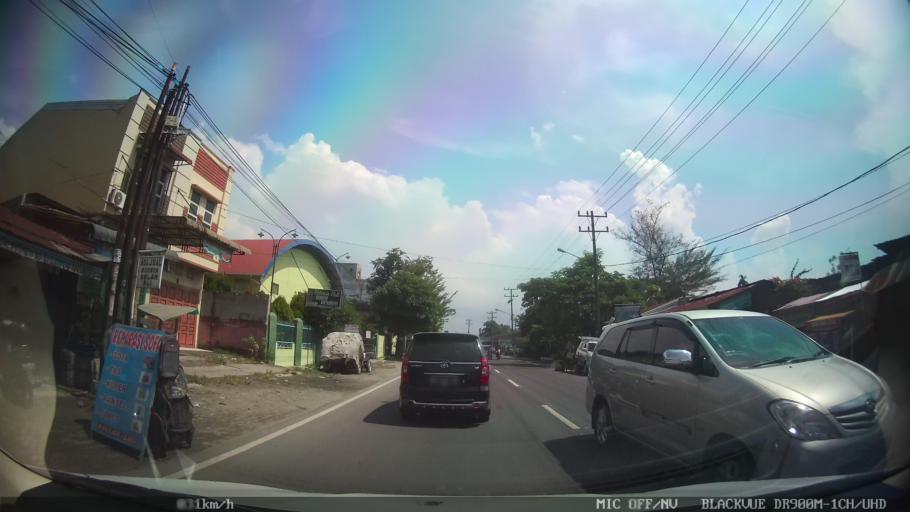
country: ID
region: North Sumatra
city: Medan
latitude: 3.6405
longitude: 98.6578
